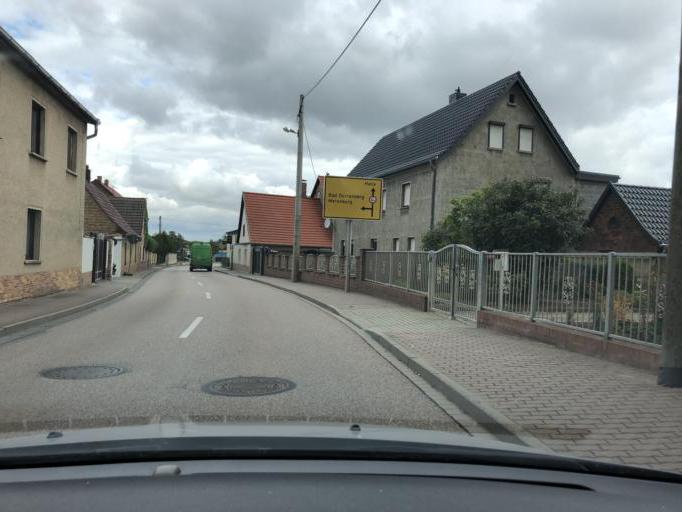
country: DE
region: Saxony-Anhalt
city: Lochau
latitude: 51.3987
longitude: 12.0517
